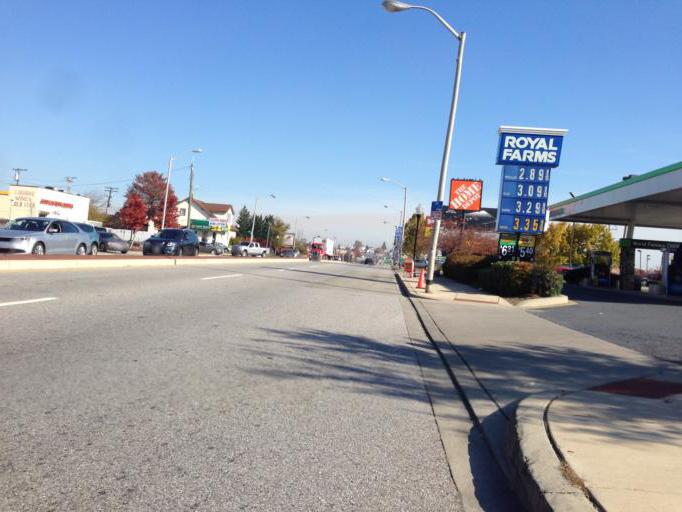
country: US
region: Maryland
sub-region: Baltimore County
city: Rosedale
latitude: 39.2876
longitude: -76.5400
